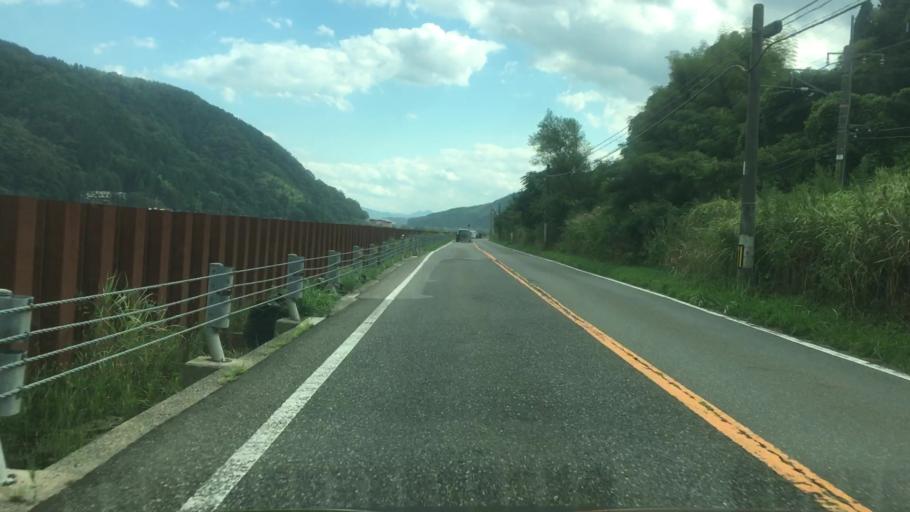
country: JP
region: Hyogo
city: Toyooka
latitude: 35.6002
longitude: 134.8017
